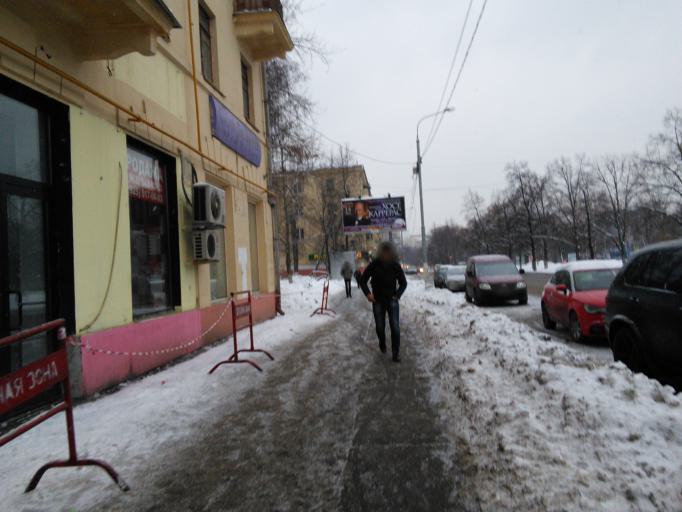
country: RU
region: Moskovskaya
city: Leninskiye Gory
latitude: 55.6892
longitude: 37.5682
